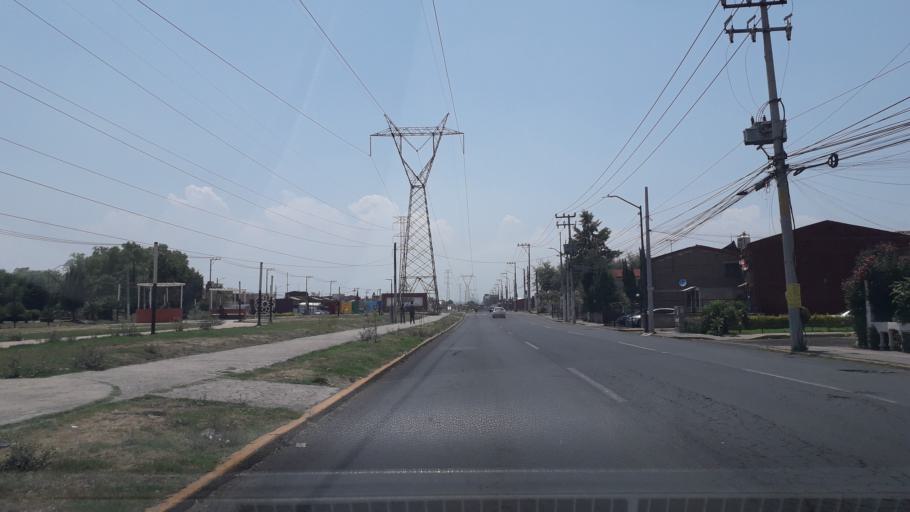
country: MX
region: Mexico
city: Santiago Teyahualco
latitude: 19.6416
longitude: -99.1229
